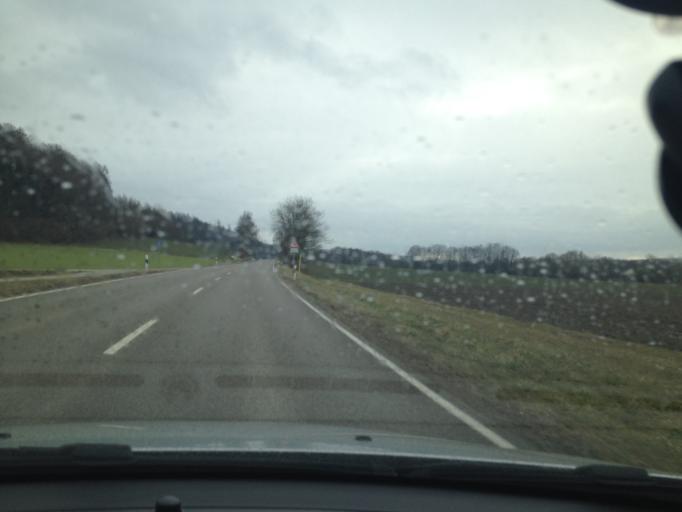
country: DE
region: Bavaria
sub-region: Swabia
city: Zusmarshausen
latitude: 48.4291
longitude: 10.5990
